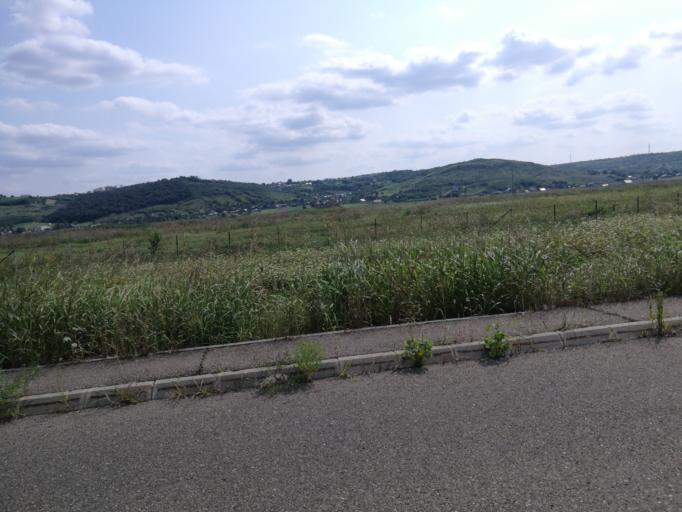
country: RO
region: Iasi
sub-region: Comuna Miroslava
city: Miroslava
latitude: 47.1663
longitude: 27.5162
